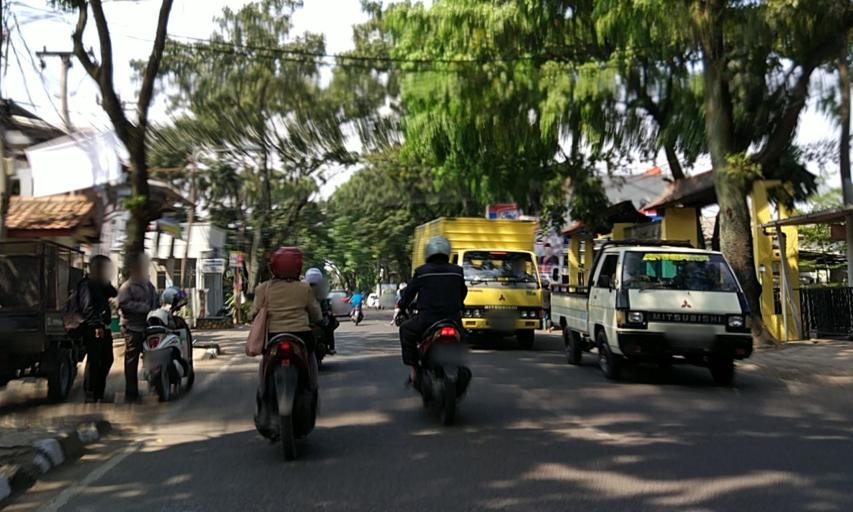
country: ID
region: West Java
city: Margahayukencana
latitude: -6.9276
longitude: 107.5683
